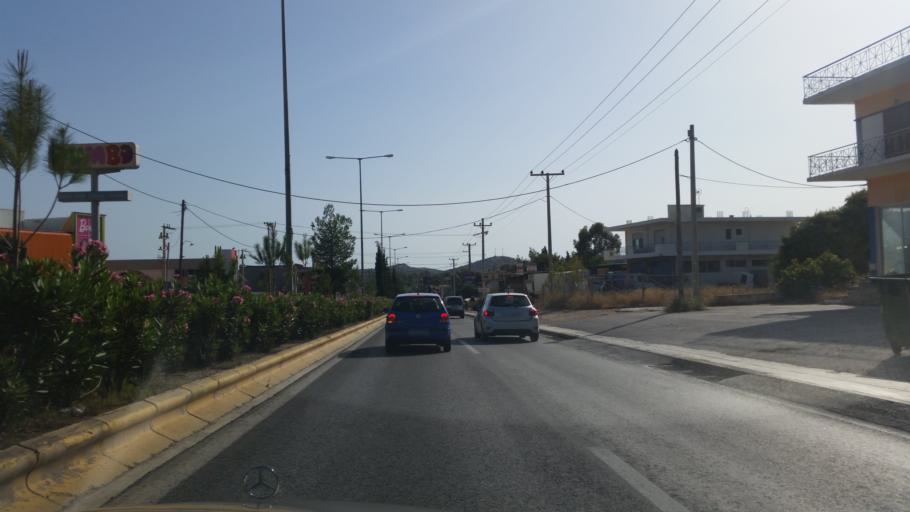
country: GR
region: Attica
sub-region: Nomarchia Anatolikis Attikis
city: Kitsi
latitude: 37.8467
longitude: 23.8246
